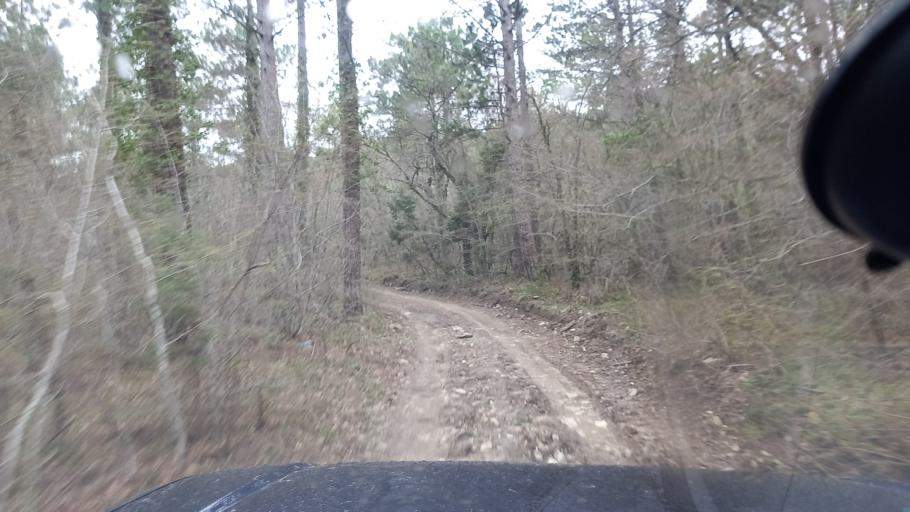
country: RU
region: Krasnodarskiy
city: Arkhipo-Osipovka
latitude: 44.3759
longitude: 38.4734
